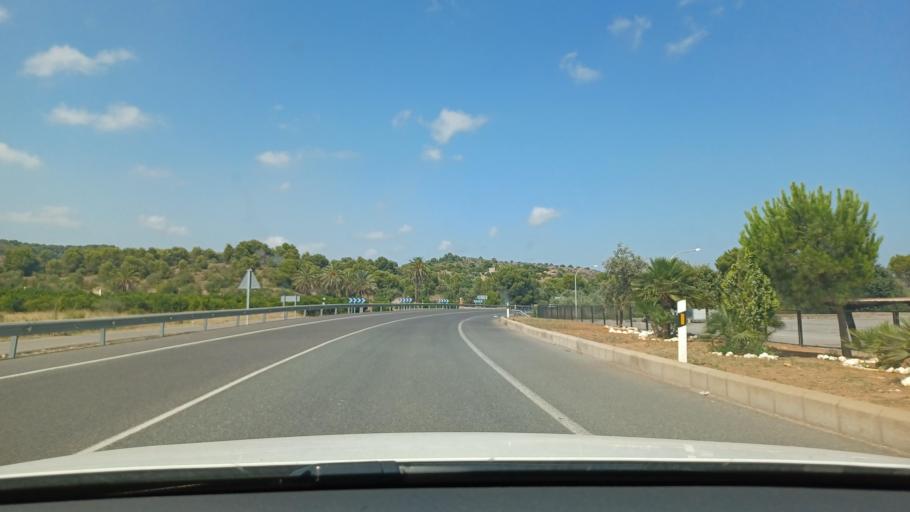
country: ES
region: Valencia
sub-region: Provincia de Castello
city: Chilches
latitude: 39.7713
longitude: -0.2070
